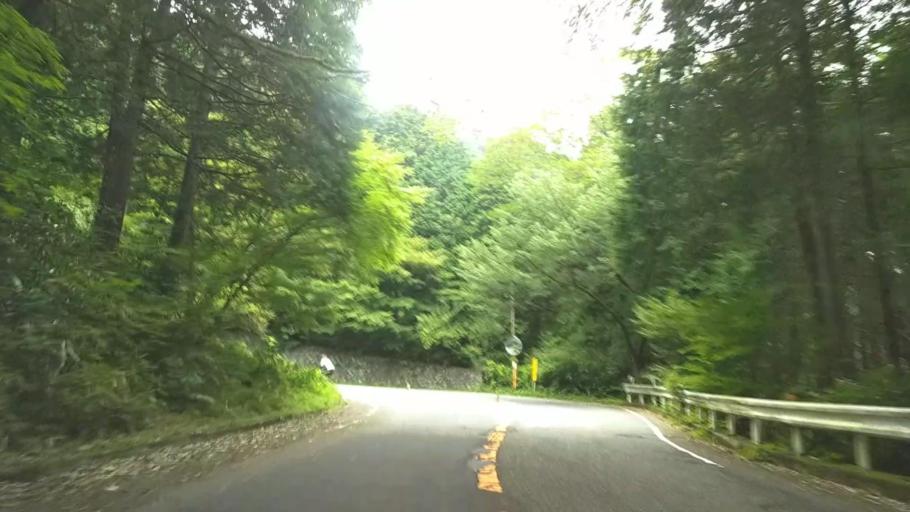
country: JP
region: Kanagawa
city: Hakone
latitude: 35.2098
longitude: 139.0606
